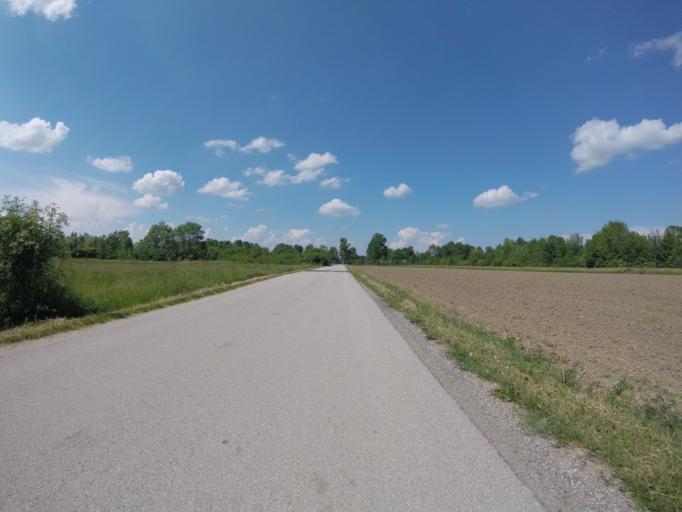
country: HR
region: Zagrebacka
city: Kuce
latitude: 45.6712
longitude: 16.1840
